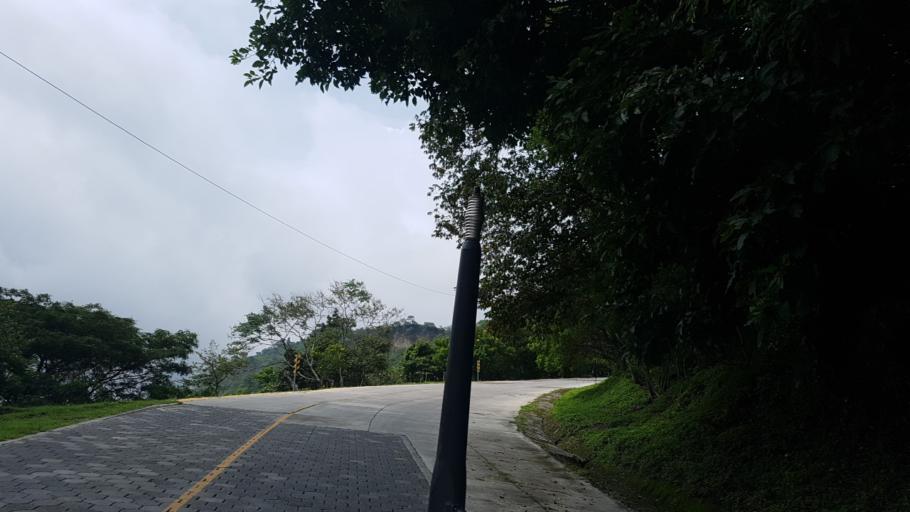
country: NI
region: Leon
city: Santa Rosa del Penon
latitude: 12.9364
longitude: -86.3397
